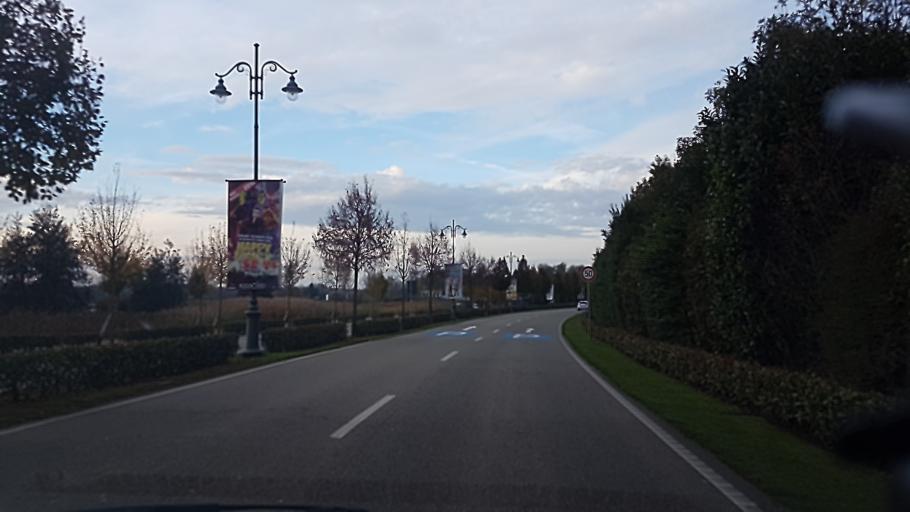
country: DE
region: Baden-Wuerttemberg
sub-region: Freiburg Region
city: Rust
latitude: 48.2617
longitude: 7.7178
